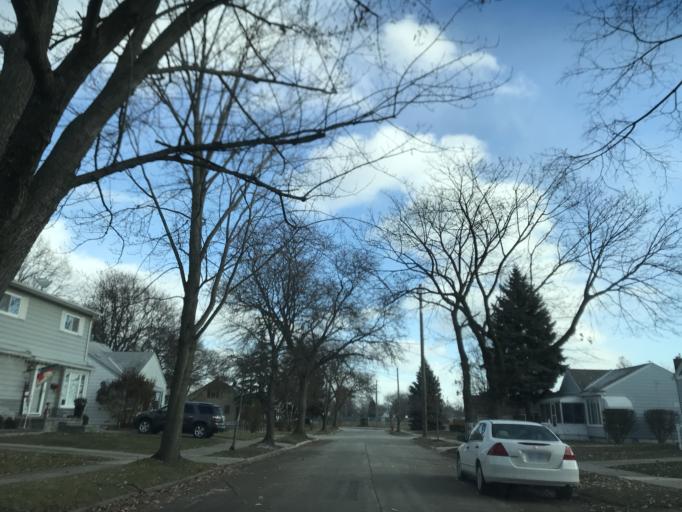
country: US
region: Michigan
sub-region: Oakland County
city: Madison Heights
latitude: 42.4788
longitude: -83.1151
